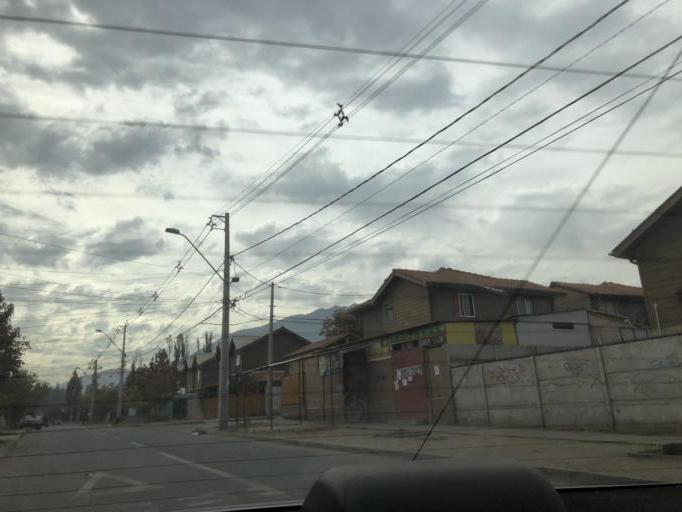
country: CL
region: Santiago Metropolitan
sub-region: Provincia de Cordillera
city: Puente Alto
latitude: -33.6118
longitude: -70.5262
